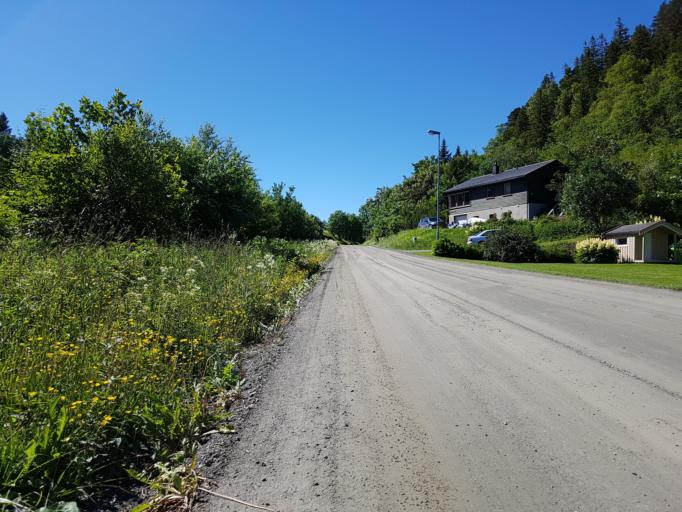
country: NO
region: Sor-Trondelag
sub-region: Skaun
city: Borsa
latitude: 63.4347
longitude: 10.1866
